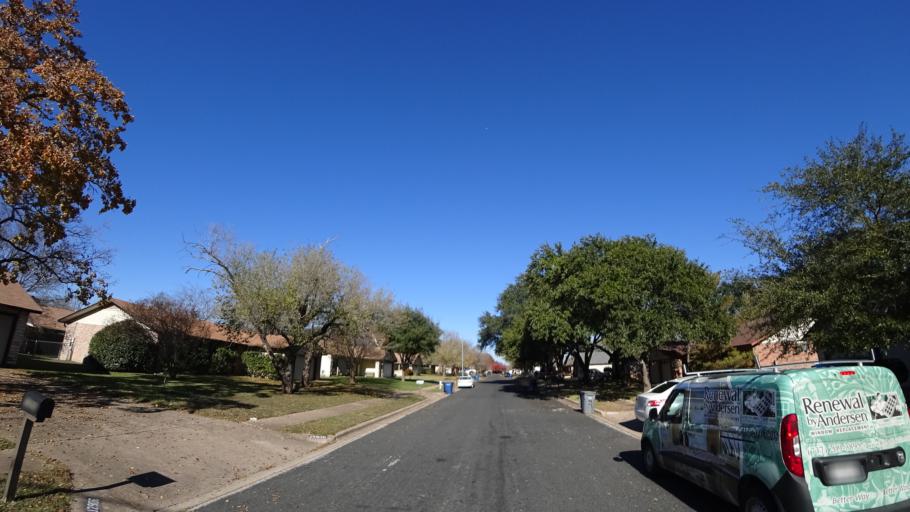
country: US
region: Texas
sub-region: Travis County
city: Wells Branch
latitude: 30.4211
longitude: -97.6908
